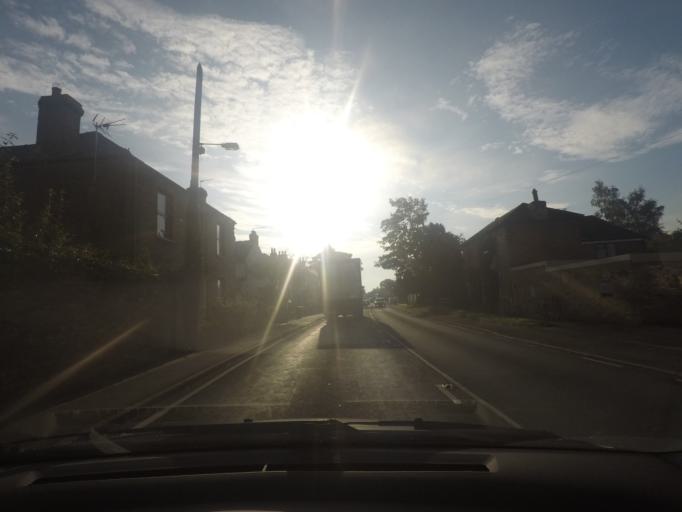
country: GB
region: England
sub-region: East Riding of Yorkshire
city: Londesborough
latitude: 53.8781
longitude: -0.7063
